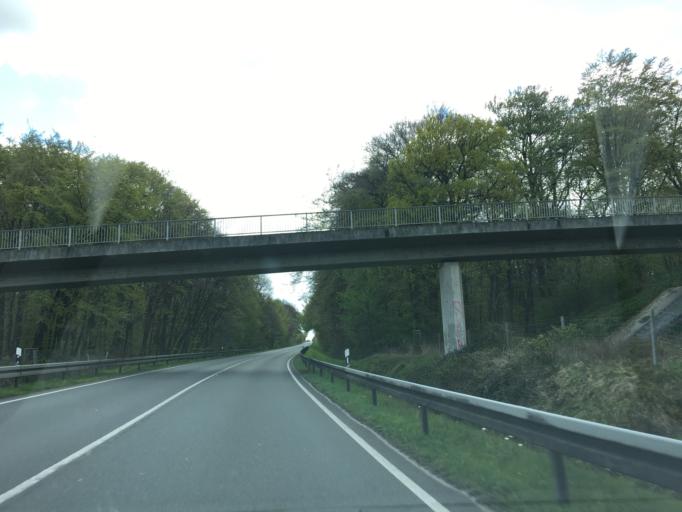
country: DE
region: North Rhine-Westphalia
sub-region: Regierungsbezirk Munster
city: Dulmen
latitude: 51.8440
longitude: 7.3120
